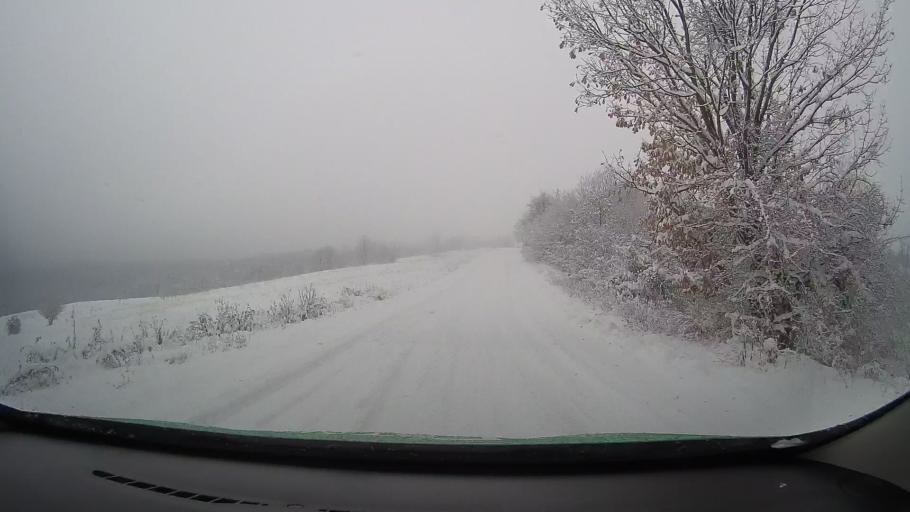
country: RO
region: Hunedoara
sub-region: Comuna Teliucu Inferior
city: Teliucu Inferior
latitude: 45.6947
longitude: 22.8933
